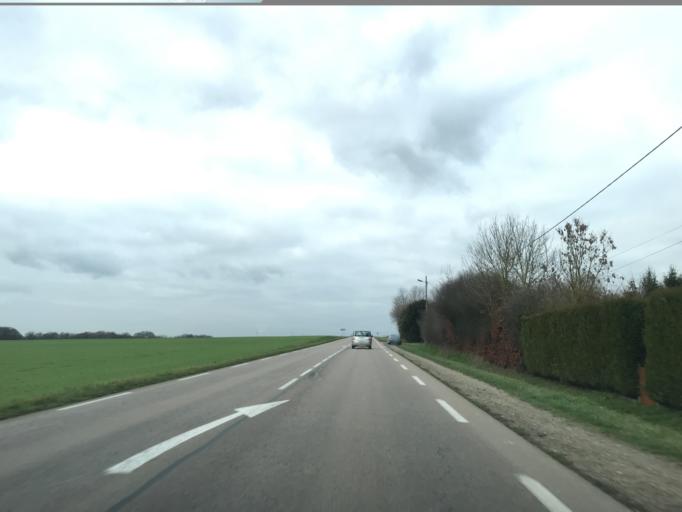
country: FR
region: Haute-Normandie
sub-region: Departement de l'Eure
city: Fleury-sur-Andelle
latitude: 49.3752
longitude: 1.3298
